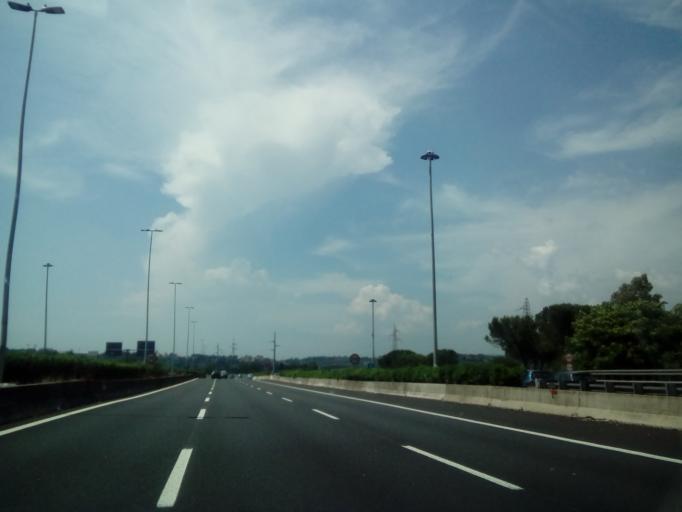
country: IT
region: Latium
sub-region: Citta metropolitana di Roma Capitale
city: Monte Caminetto
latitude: 41.9888
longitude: 12.5138
